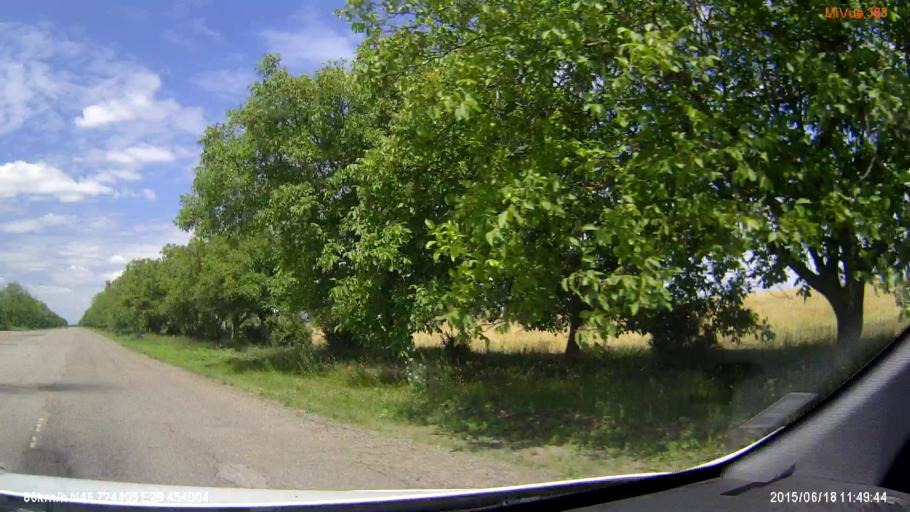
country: MD
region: Causeni
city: Causeni
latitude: 46.7240
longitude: 29.4541
